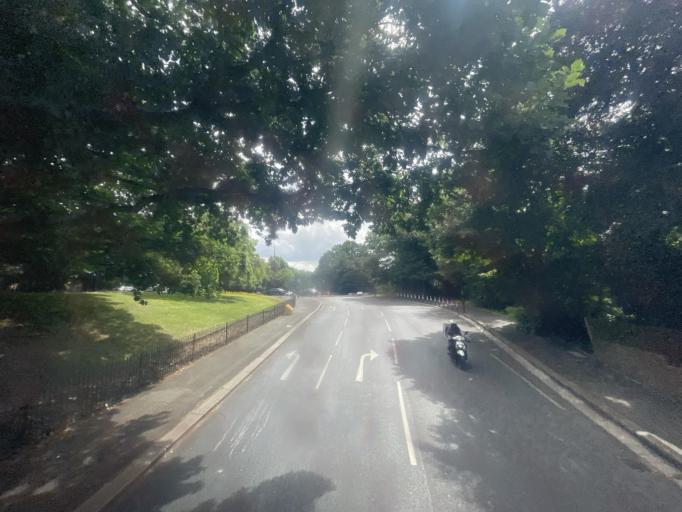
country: GB
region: England
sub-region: Greater London
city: Thornton Heath
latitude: 51.4248
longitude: -0.0760
